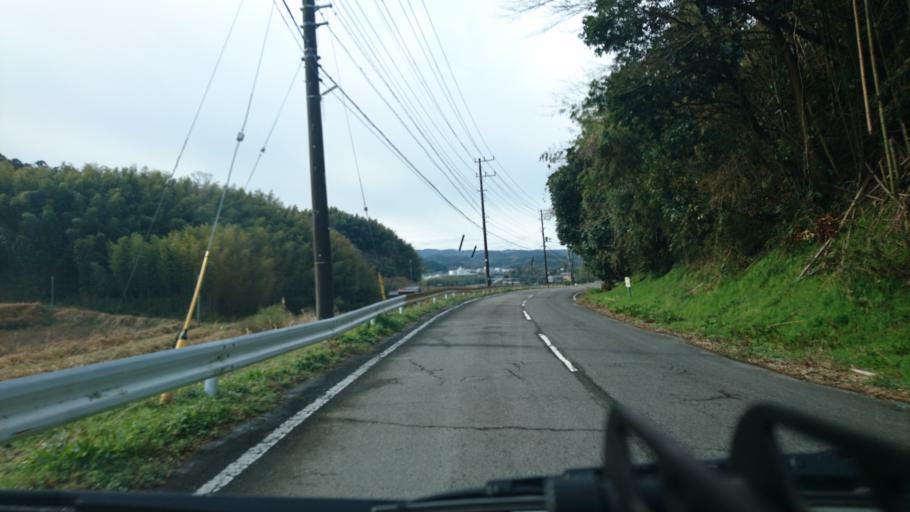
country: JP
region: Chiba
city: Kisarazu
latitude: 35.3159
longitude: 139.9639
